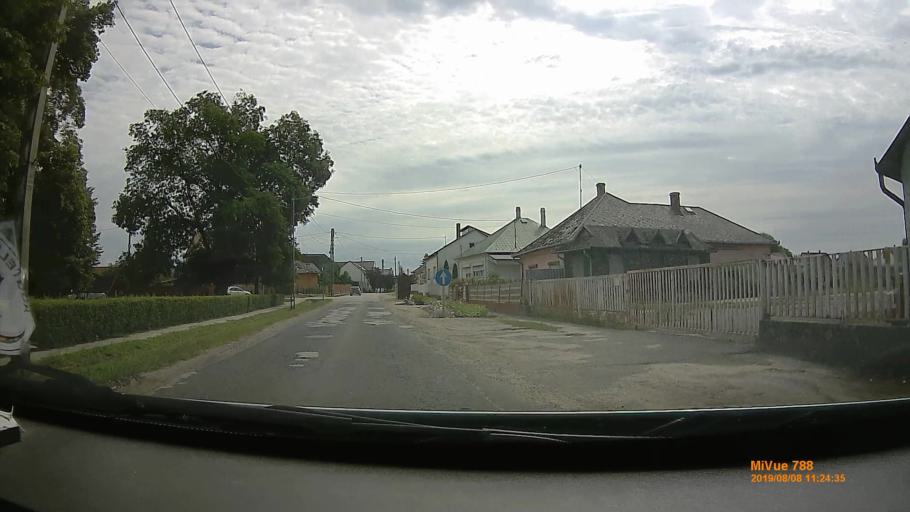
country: HU
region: Szabolcs-Szatmar-Bereg
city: Balkany
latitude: 47.7706
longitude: 21.8556
